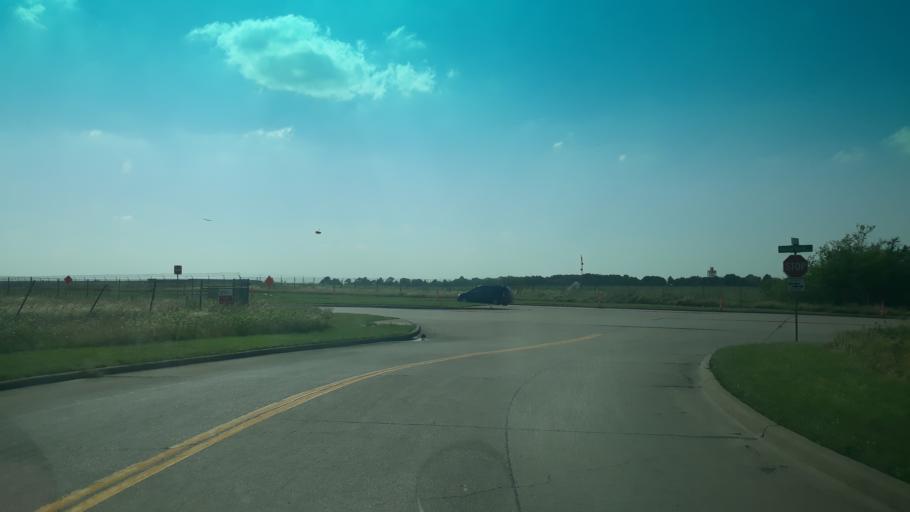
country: US
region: Texas
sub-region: Dallas County
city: Irving
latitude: 32.8706
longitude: -97.0065
